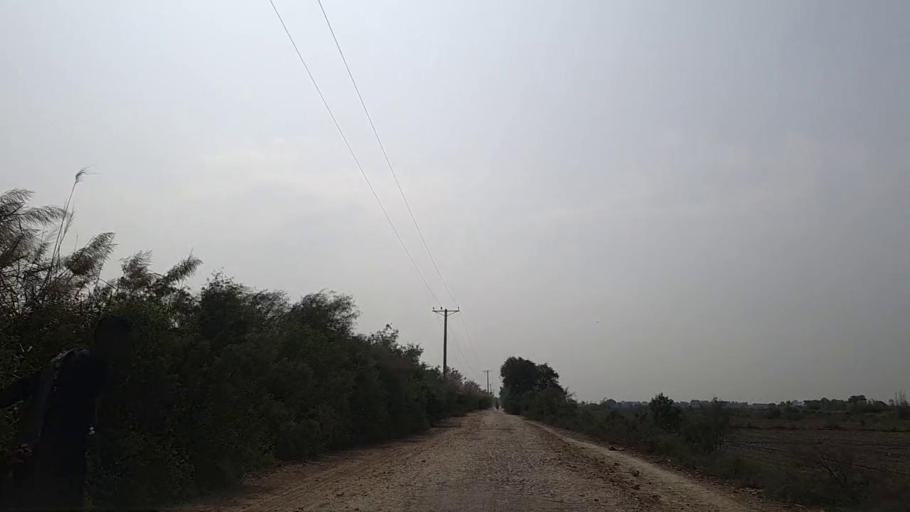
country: PK
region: Sindh
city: Mirpur Sakro
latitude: 24.6312
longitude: 67.7468
